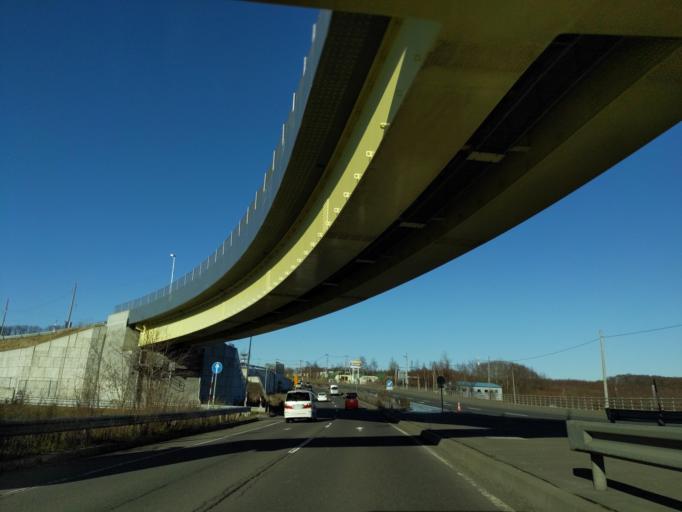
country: JP
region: Hokkaido
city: Kitahiroshima
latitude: 42.9555
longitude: 141.4959
